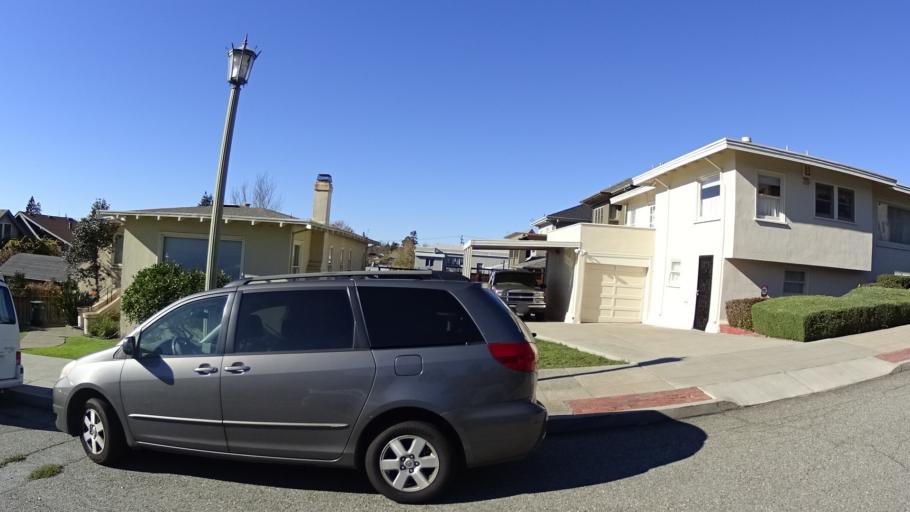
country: US
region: California
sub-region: Alameda County
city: Piedmont
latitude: 37.8435
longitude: -122.2447
